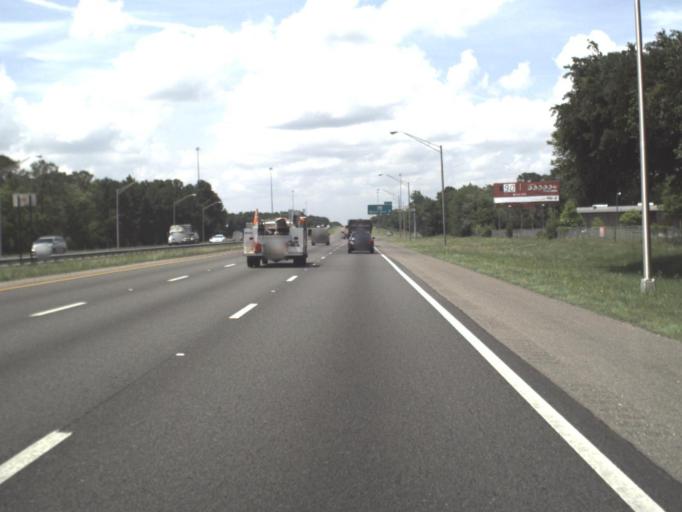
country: US
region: Florida
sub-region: Clay County
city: Bellair-Meadowbrook Terrace
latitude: 30.2639
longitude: -81.7648
